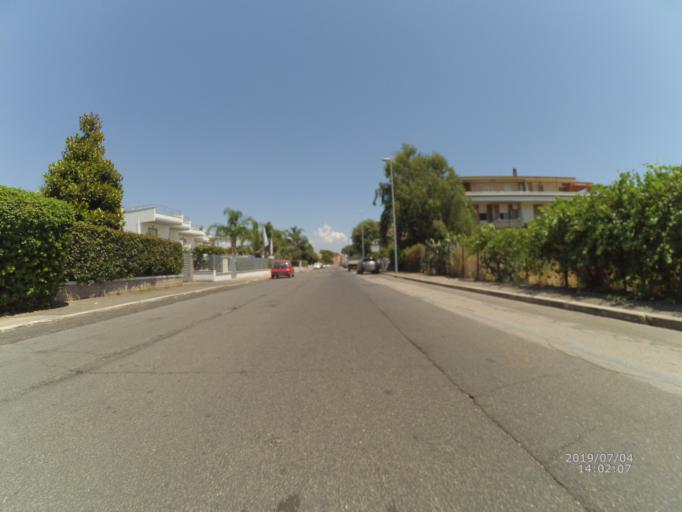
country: IT
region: Latium
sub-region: Provincia di Latina
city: Terracina
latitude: 41.2863
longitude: 13.2322
